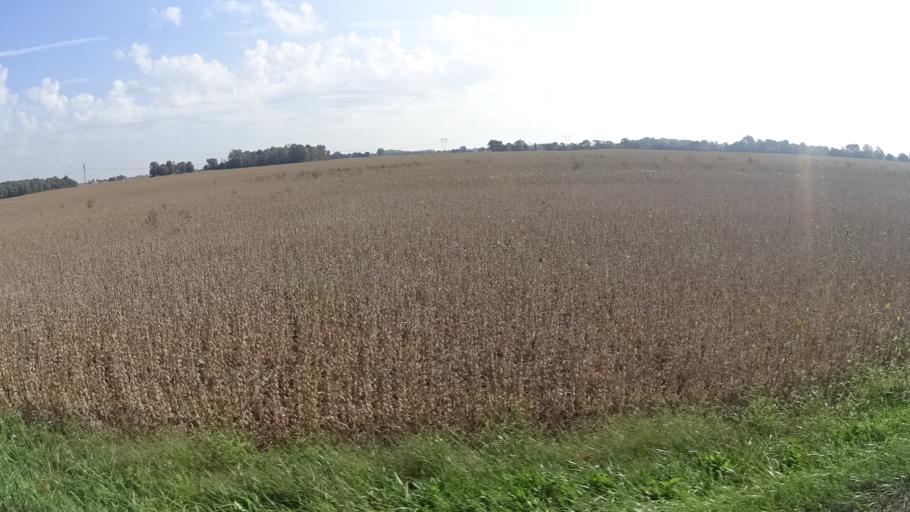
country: US
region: Indiana
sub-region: Madison County
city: Lapel
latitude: 40.0281
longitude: -85.8624
